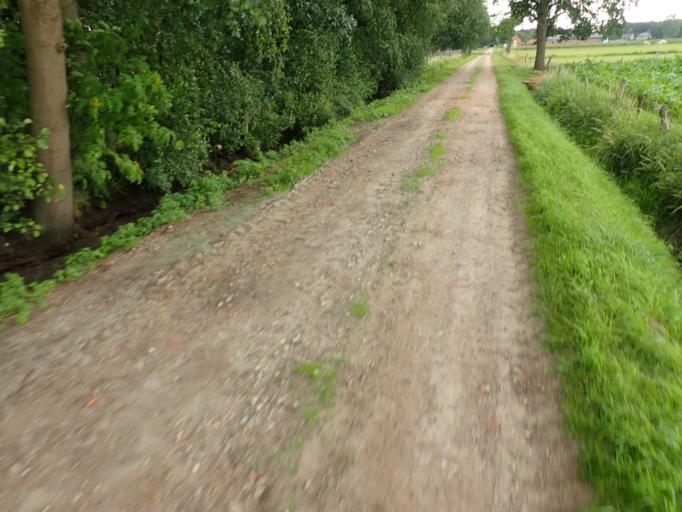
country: BE
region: Flanders
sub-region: Provincie Antwerpen
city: Oostmalle
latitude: 51.3062
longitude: 4.7645
